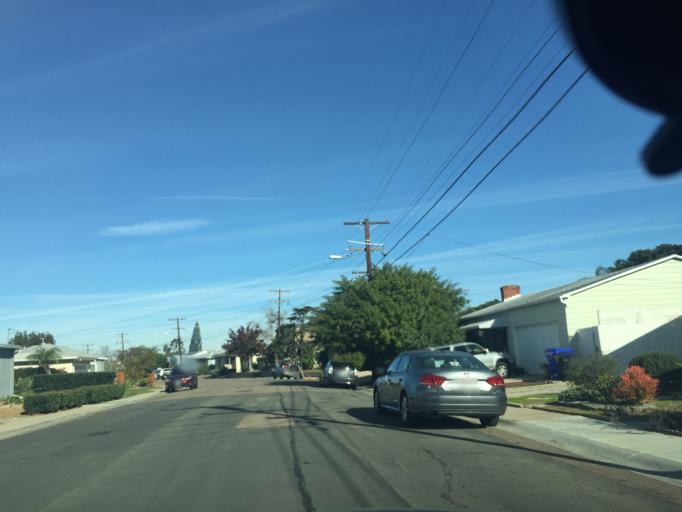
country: US
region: California
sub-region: San Diego County
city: Lemon Grove
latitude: 32.7641
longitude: -117.0809
